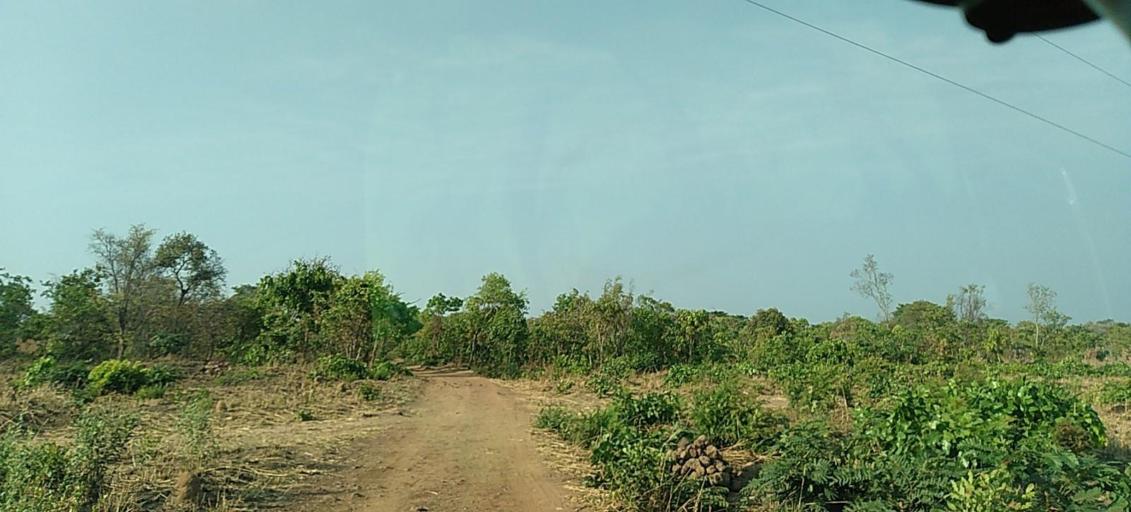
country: ZM
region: North-Western
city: Kalengwa
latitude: -13.1527
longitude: 25.0342
